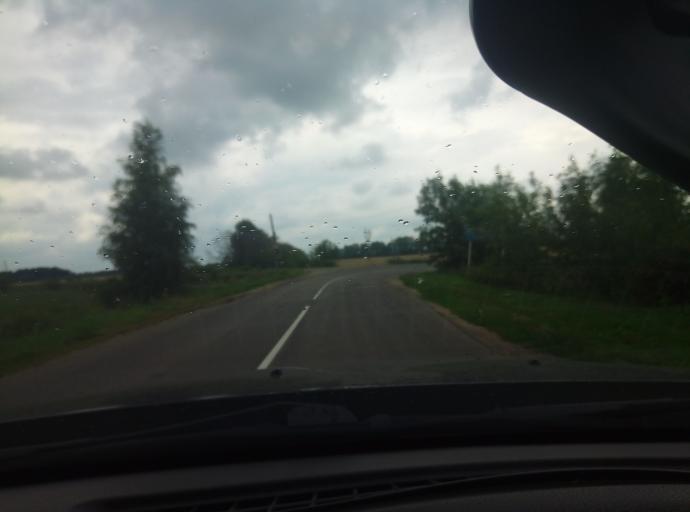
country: RU
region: Tula
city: Begichevskiy
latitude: 53.8507
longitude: 38.2300
